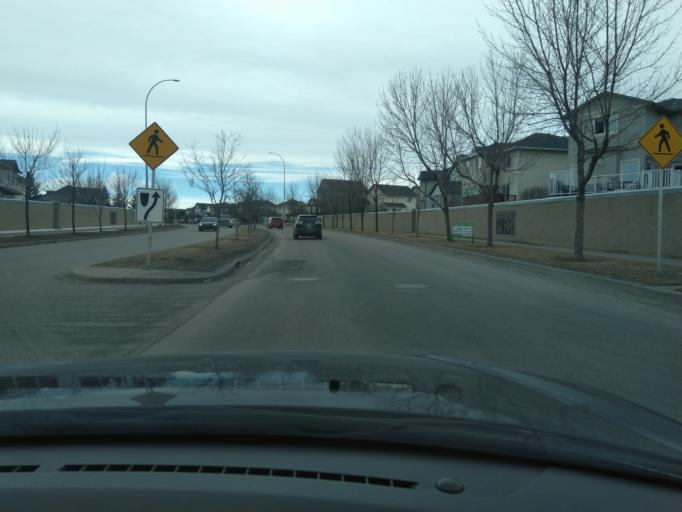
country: CA
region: Alberta
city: Calgary
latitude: 51.1648
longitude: -114.0723
